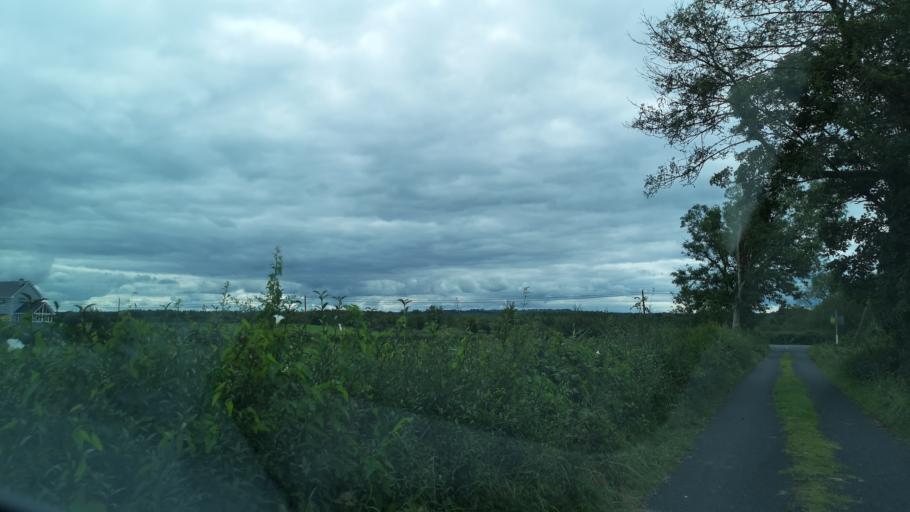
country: IE
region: Connaught
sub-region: County Galway
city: Loughrea
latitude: 53.1547
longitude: -8.4366
